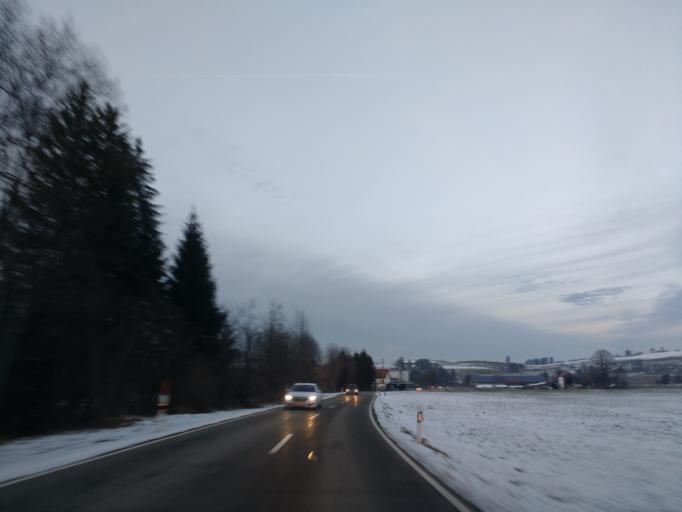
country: DE
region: Bavaria
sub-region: Swabia
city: Halblech
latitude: 47.6387
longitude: 10.8168
